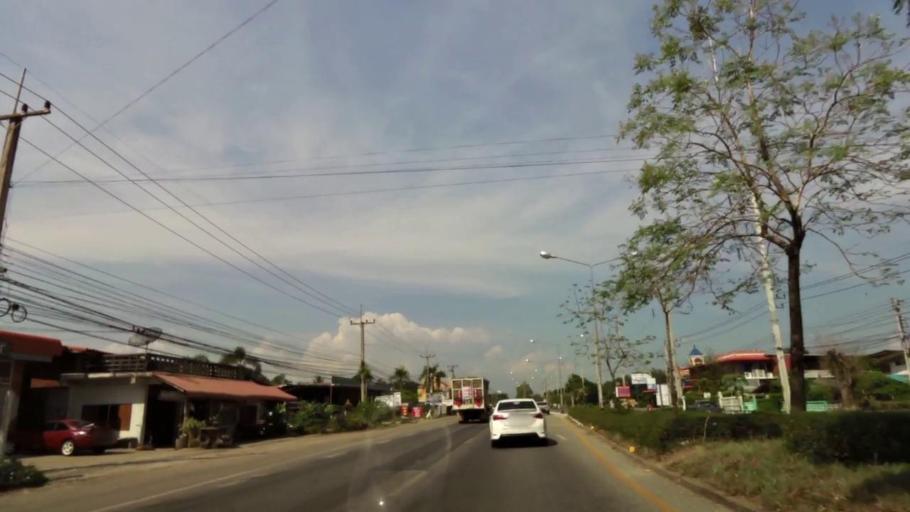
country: TH
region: Uttaradit
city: Uttaradit
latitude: 17.5914
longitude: 100.1327
